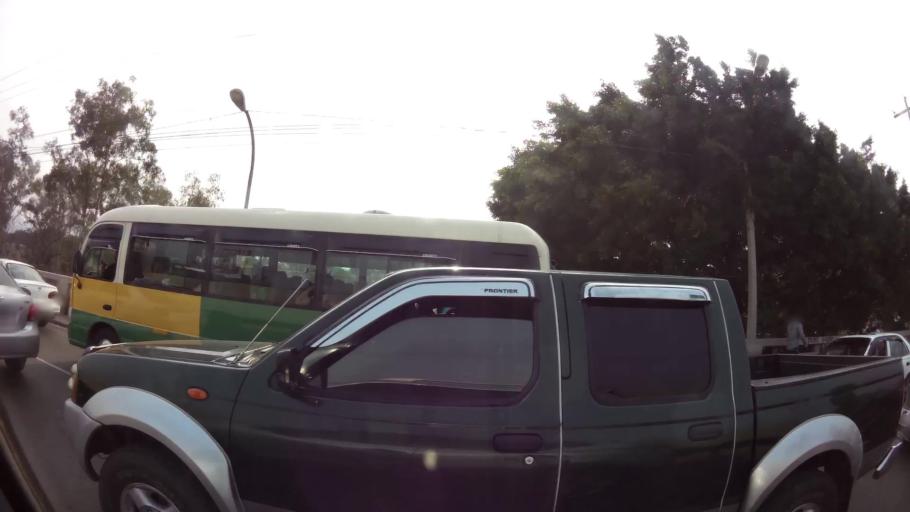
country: HN
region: Francisco Morazan
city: Tegucigalpa
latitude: 14.0750
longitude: -87.1849
